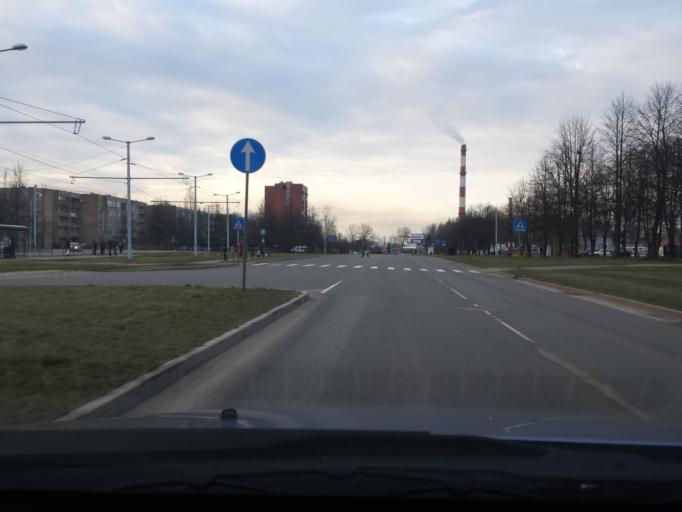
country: LV
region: Marupe
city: Marupe
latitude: 56.9563
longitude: 24.0351
